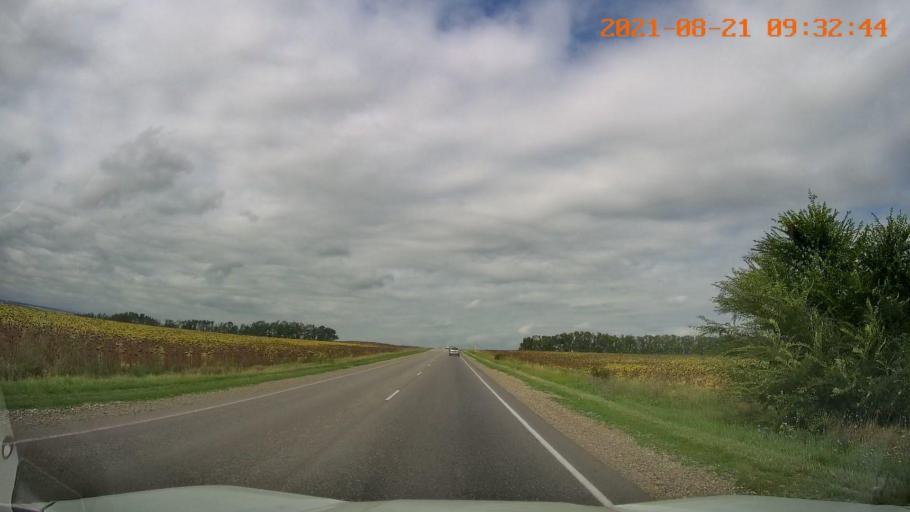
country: RU
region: Stavropol'skiy
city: Yutsa
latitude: 43.9928
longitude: 43.0008
